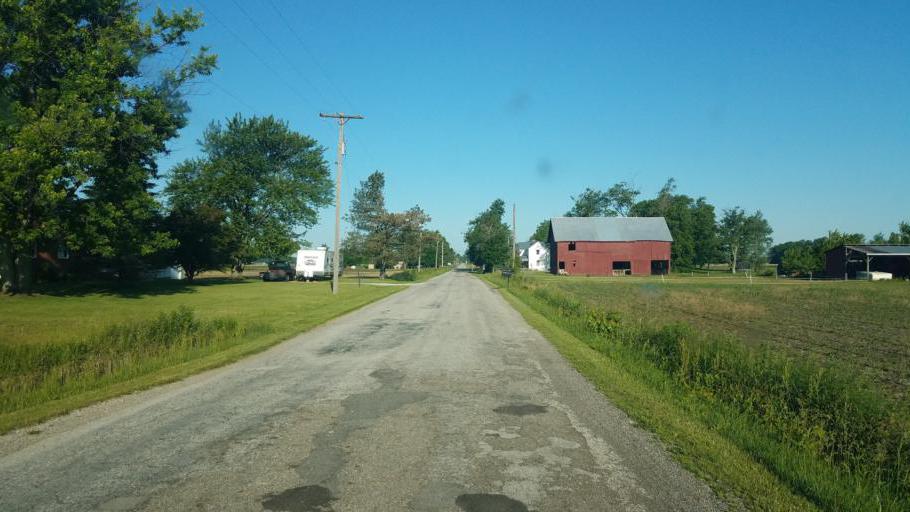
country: US
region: Ohio
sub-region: Morrow County
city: Mount Gilead
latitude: 40.6161
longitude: -82.9151
